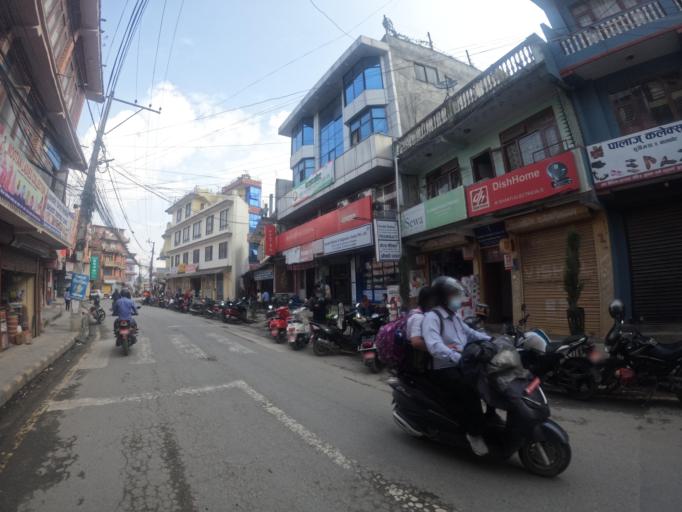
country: NP
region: Central Region
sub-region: Bagmati Zone
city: Patan
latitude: 27.6652
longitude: 85.3666
